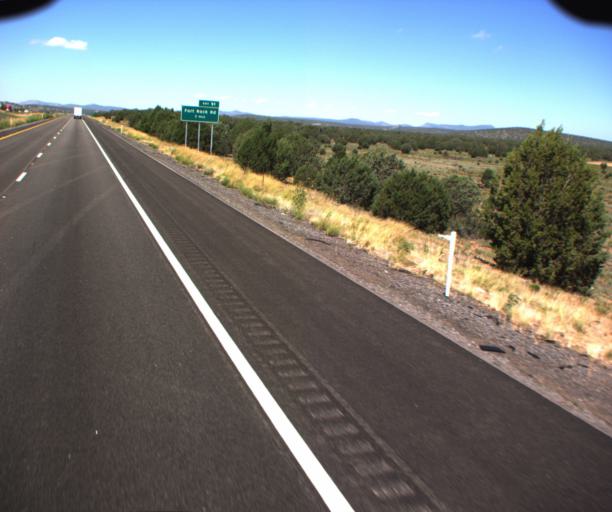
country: US
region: Arizona
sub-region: Mohave County
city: Peach Springs
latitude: 35.1912
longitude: -113.3430
